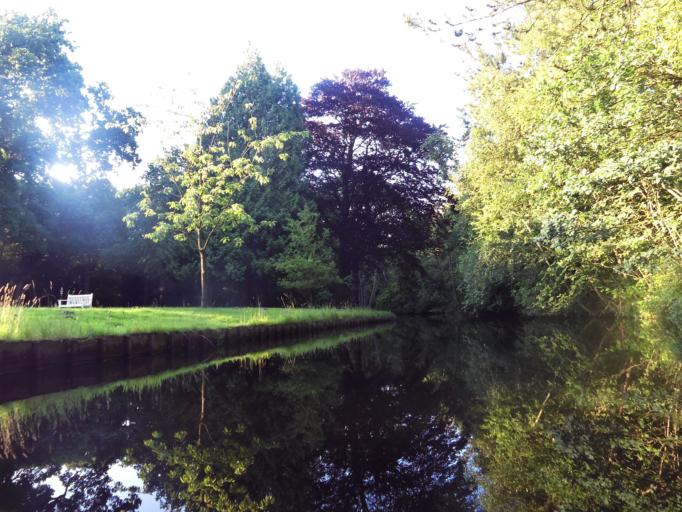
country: NL
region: South Holland
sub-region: Gemeente Wassenaar
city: Wassenaar
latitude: 52.1361
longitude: 4.3869
